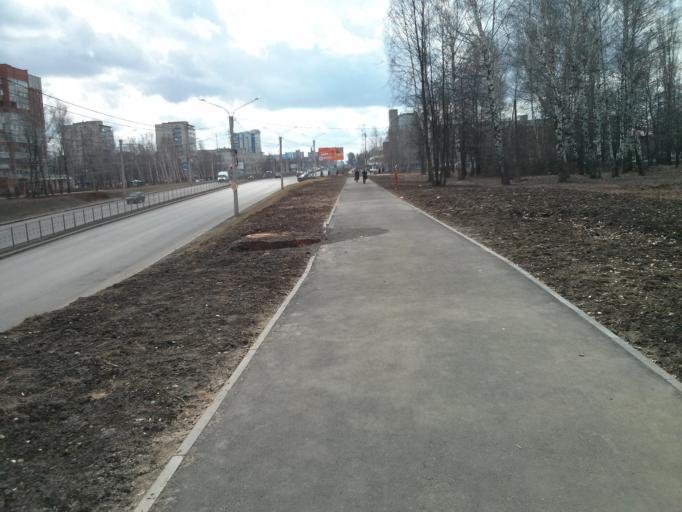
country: RU
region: Chuvashia
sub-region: Cheboksarskiy Rayon
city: Cheboksary
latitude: 56.1084
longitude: 47.2604
